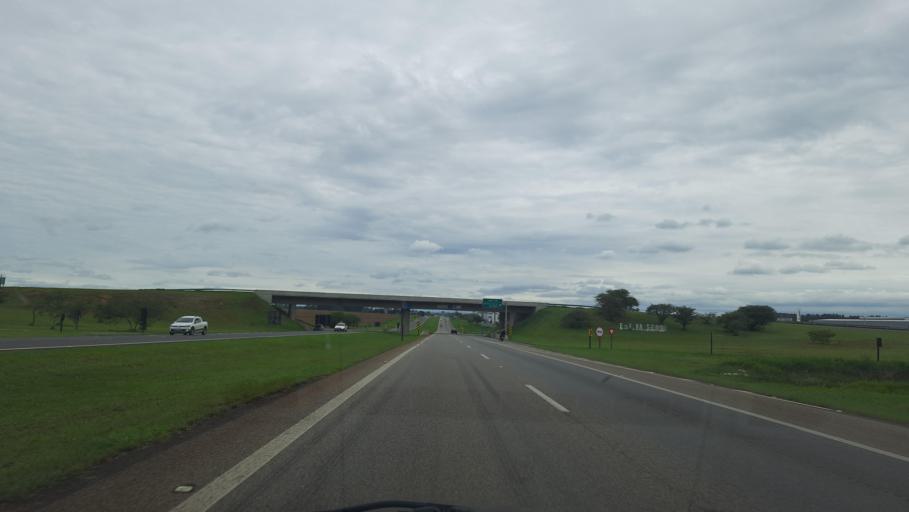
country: BR
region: Sao Paulo
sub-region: Moji-Guacu
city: Mogi-Gaucu
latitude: -22.2926
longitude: -46.9702
